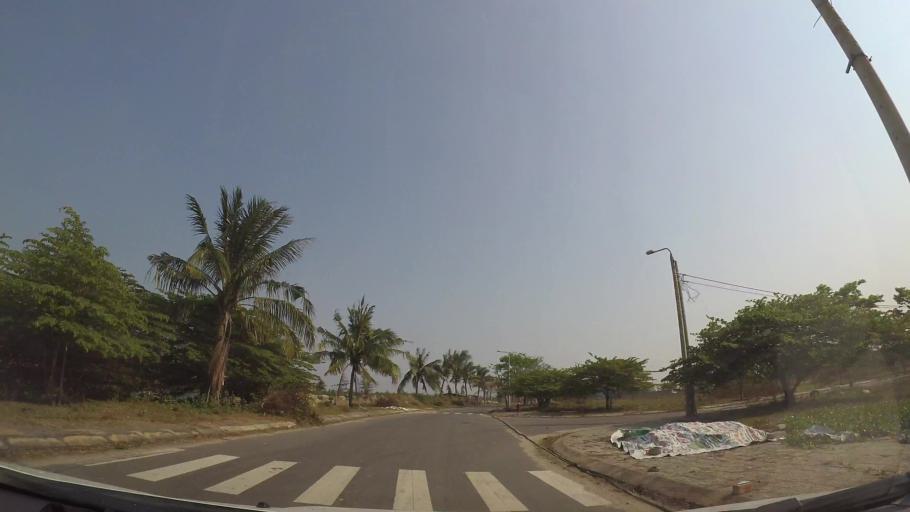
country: VN
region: Da Nang
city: Ngu Hanh Son
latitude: 15.9573
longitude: 108.2825
